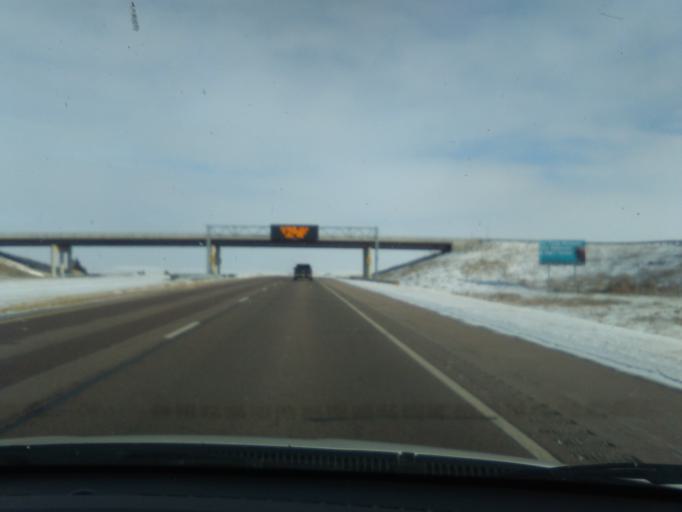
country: US
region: Nebraska
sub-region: Kimball County
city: Kimball
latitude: 41.2048
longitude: -103.7216
